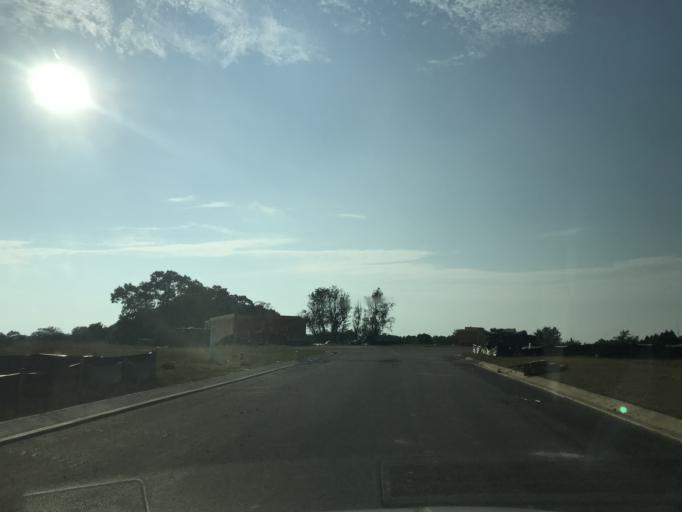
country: US
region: Maryland
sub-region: Carroll County
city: Westminster
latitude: 39.5568
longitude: -76.9766
